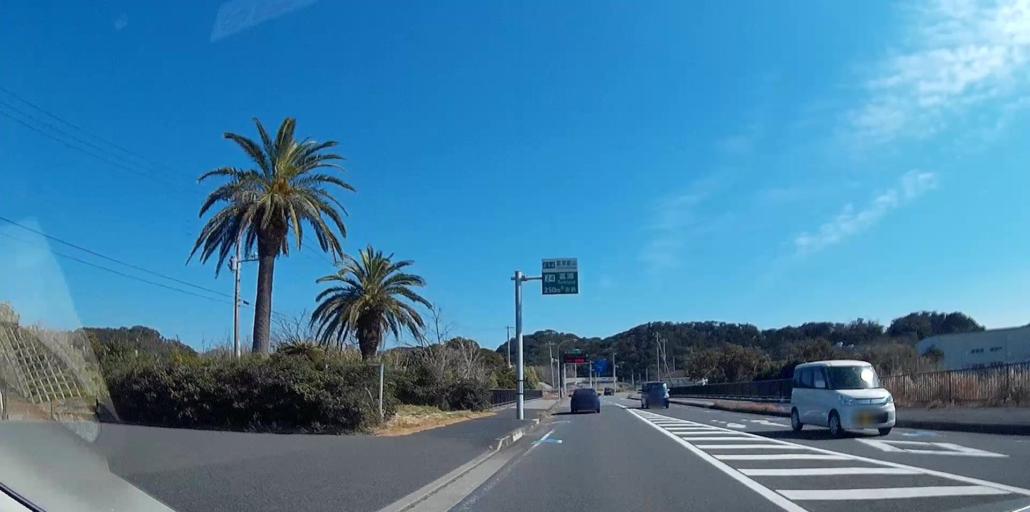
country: JP
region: Chiba
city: Tateyama
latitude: 35.0390
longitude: 139.8479
